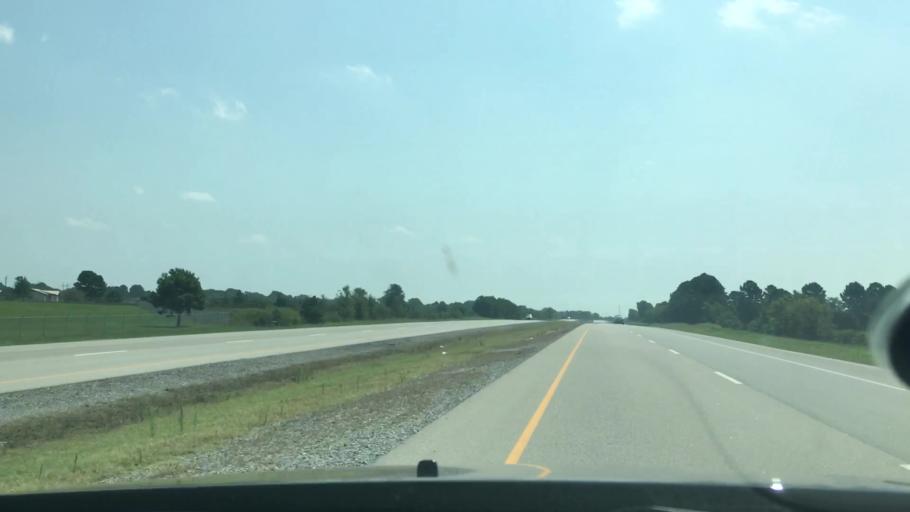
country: US
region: Oklahoma
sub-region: Atoka County
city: Atoka
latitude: 34.3421
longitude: -96.0697
